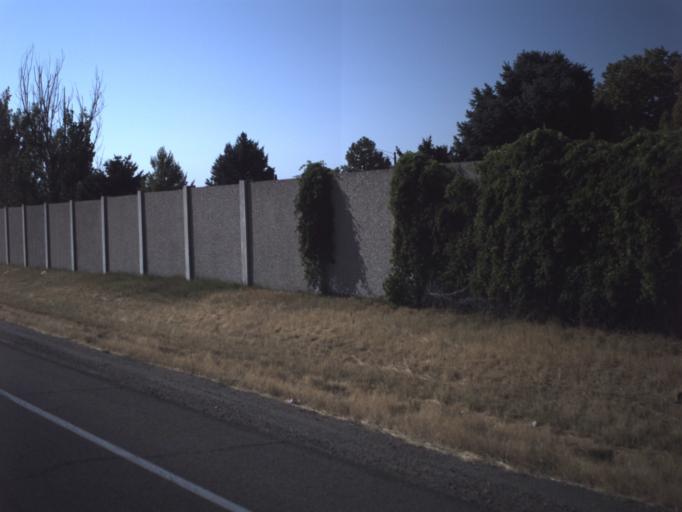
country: US
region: Utah
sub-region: Davis County
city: Hill Air Force Bace
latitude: 41.0884
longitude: -111.9910
